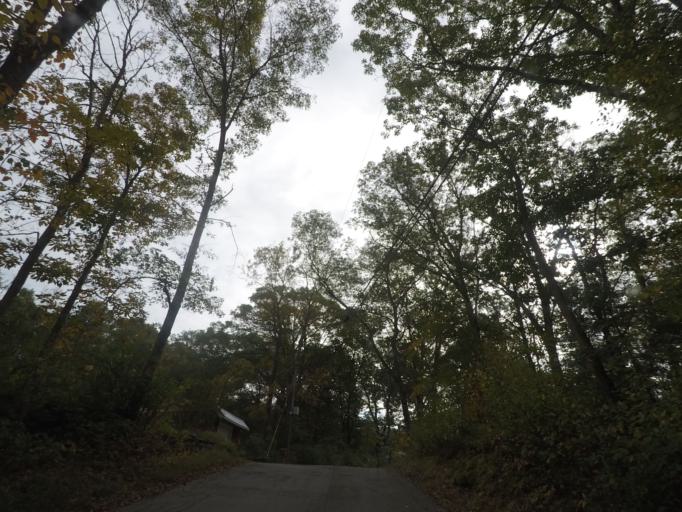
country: US
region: Connecticut
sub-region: Windham County
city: Thompson
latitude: 41.9744
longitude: -71.8405
